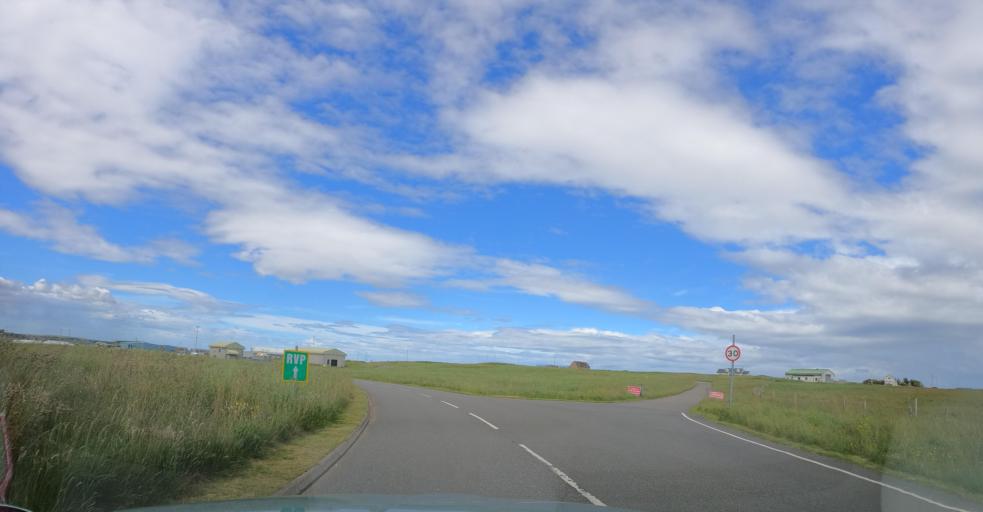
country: GB
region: Scotland
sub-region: Eilean Siar
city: Stornoway
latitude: 58.2114
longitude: -6.3218
